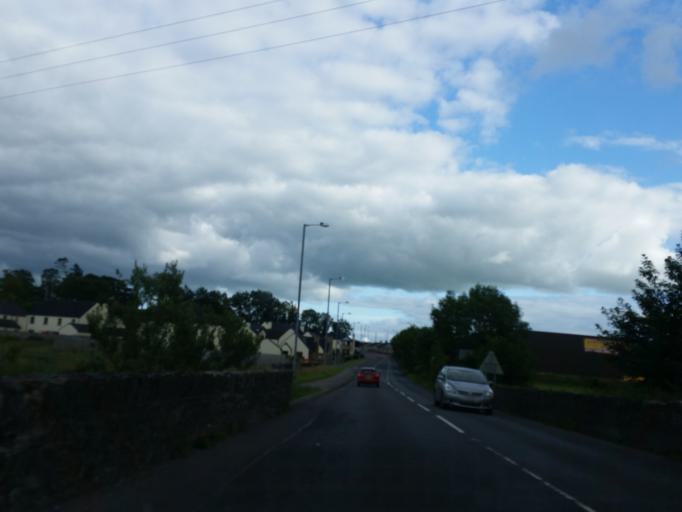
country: GB
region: Northern Ireland
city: Lisnaskea
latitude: 54.2633
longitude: -7.4612
